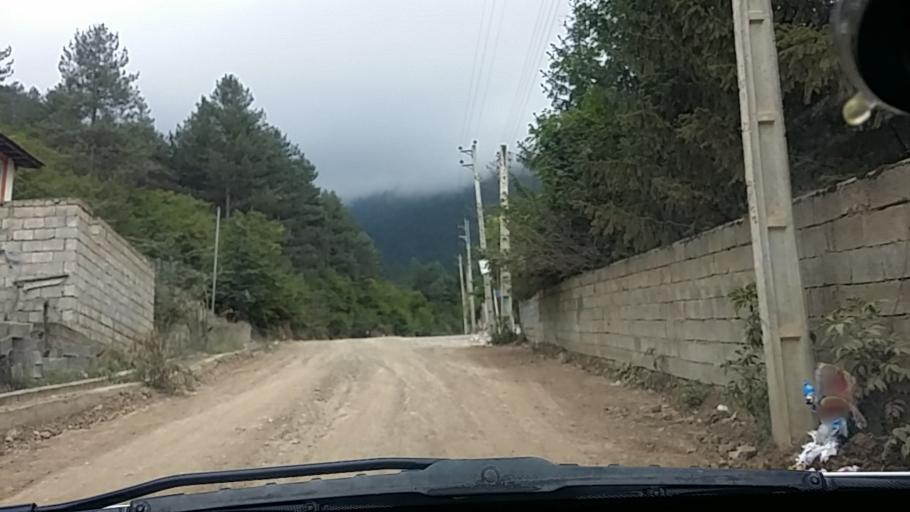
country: IR
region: Mazandaran
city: `Abbasabad
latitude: 36.4923
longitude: 51.1664
